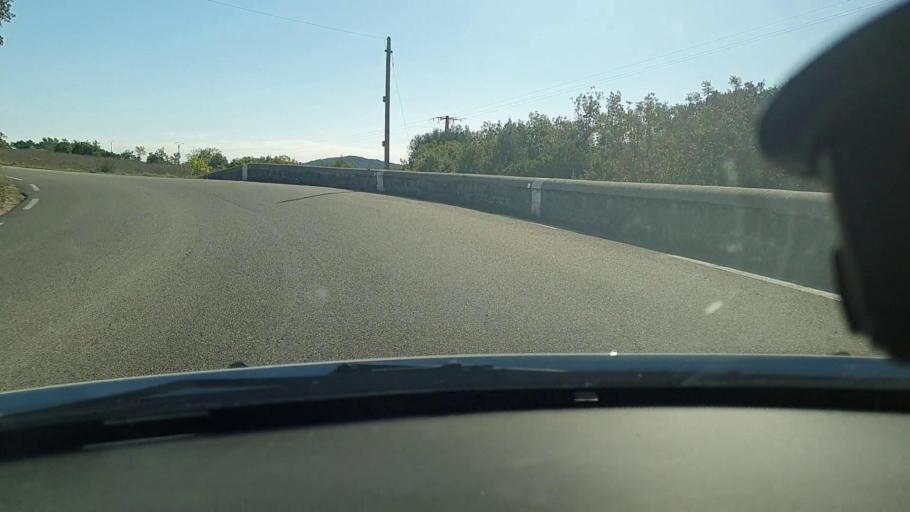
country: FR
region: Languedoc-Roussillon
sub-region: Departement du Gard
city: Saint-Julien-de-Peyrolas
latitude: 44.2969
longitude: 4.5289
